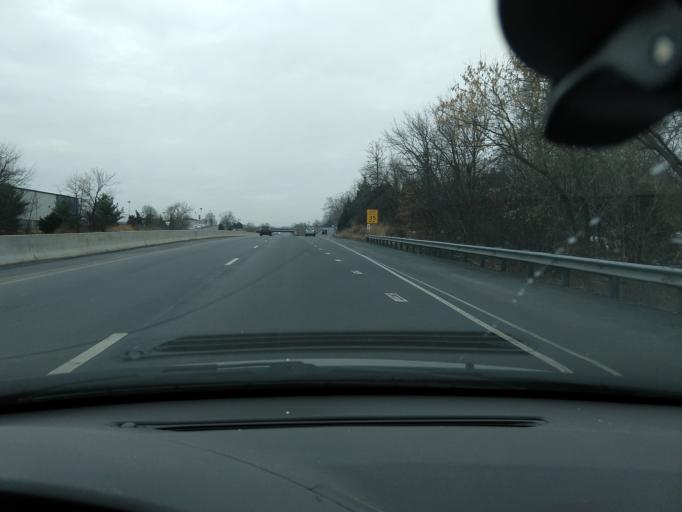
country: US
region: Pennsylvania
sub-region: Montgomery County
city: Gilbertsville
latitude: 40.3303
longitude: -75.6215
